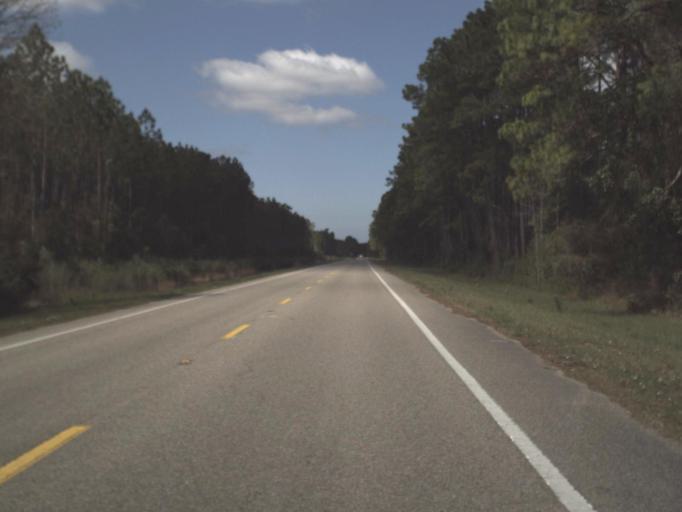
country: US
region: Florida
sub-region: Gulf County
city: Port Saint Joe
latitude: 29.7357
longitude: -85.1579
